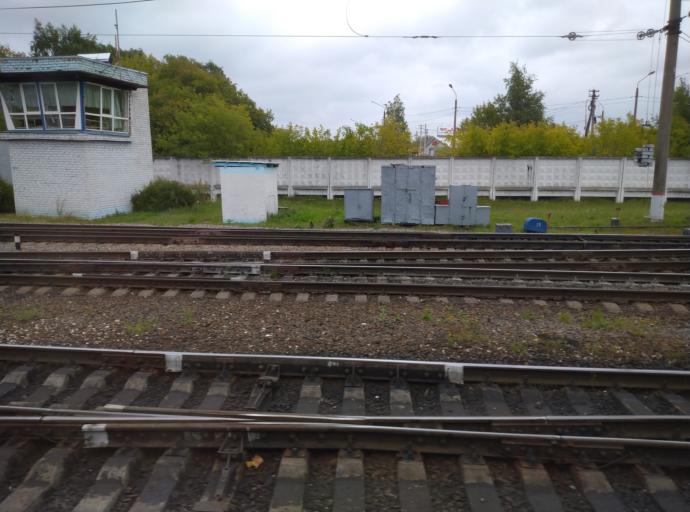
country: RU
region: Kostroma
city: Oktyabr'skiy
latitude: 57.7563
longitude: 40.9797
